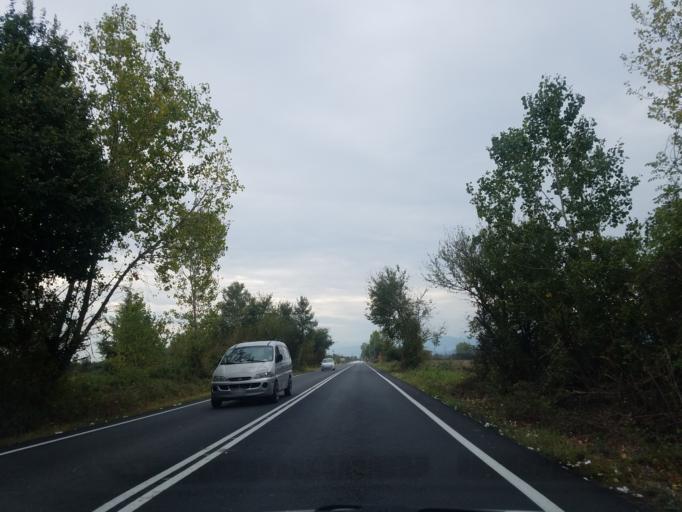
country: GR
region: Thessaly
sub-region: Nomos Kardhitsas
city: Agnantero
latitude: 39.4963
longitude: 21.8386
